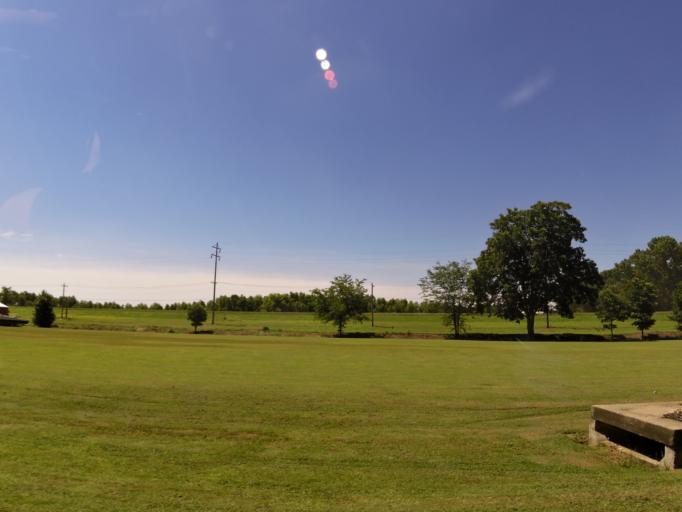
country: US
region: Missouri
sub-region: New Madrid County
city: New Madrid
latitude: 36.5842
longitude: -89.5393
